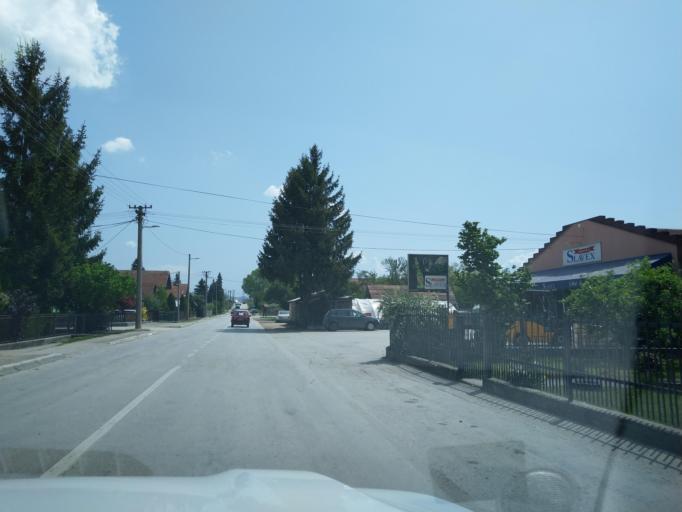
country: RS
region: Central Serbia
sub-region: Zlatiborski Okrug
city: Pozega
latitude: 43.8470
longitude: 20.0178
